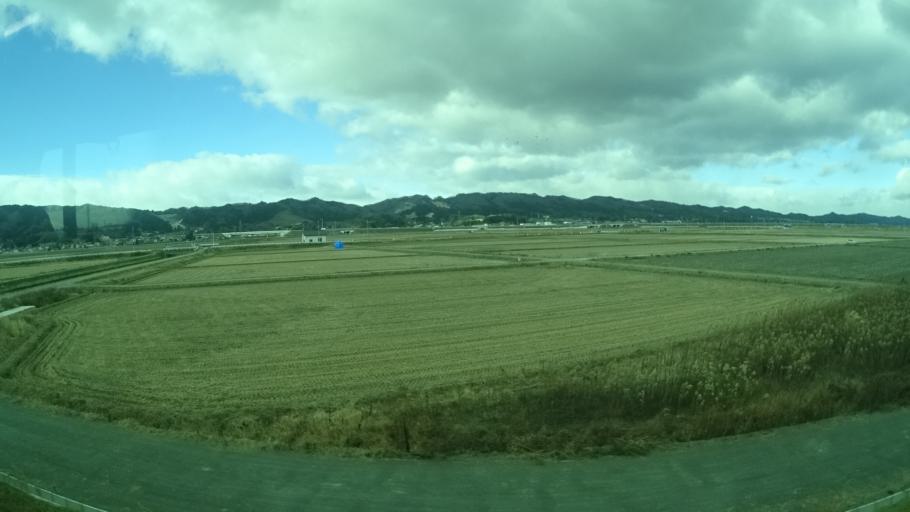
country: JP
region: Miyagi
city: Watari
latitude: 37.9793
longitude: 140.8872
